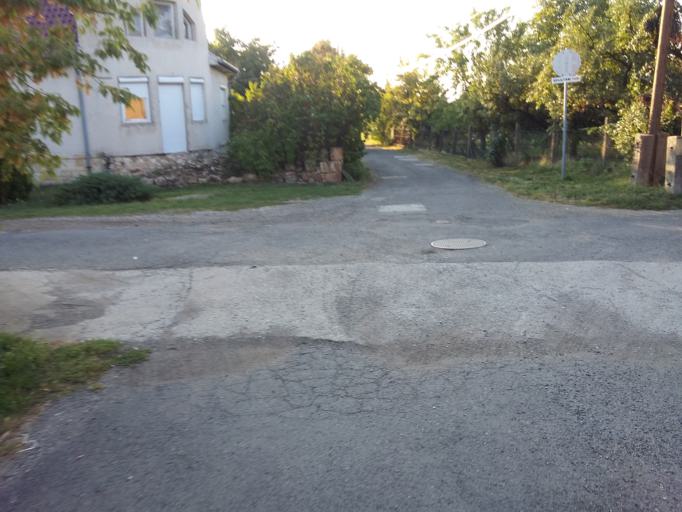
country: HU
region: Borsod-Abauj-Zemplen
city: Bekecs
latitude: 48.1591
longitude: 21.1802
